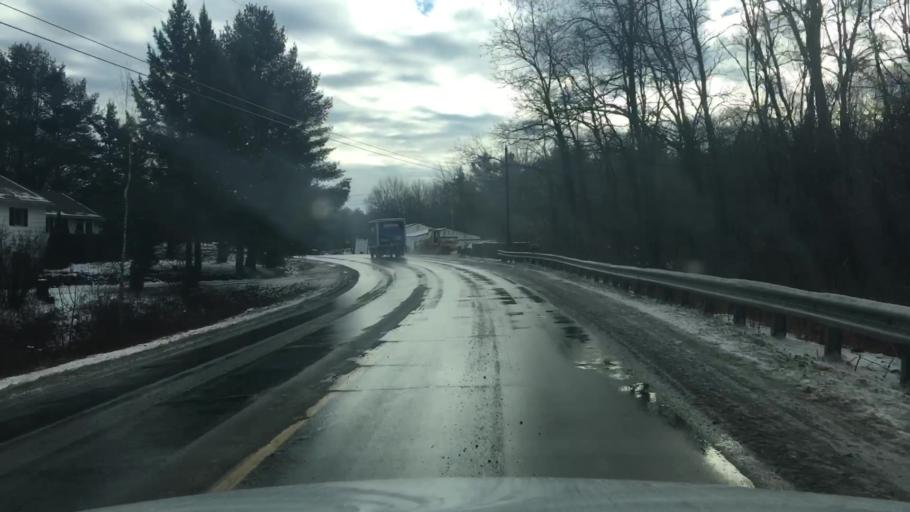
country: US
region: Maine
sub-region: Penobscot County
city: Brewer
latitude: 44.7604
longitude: -68.7739
